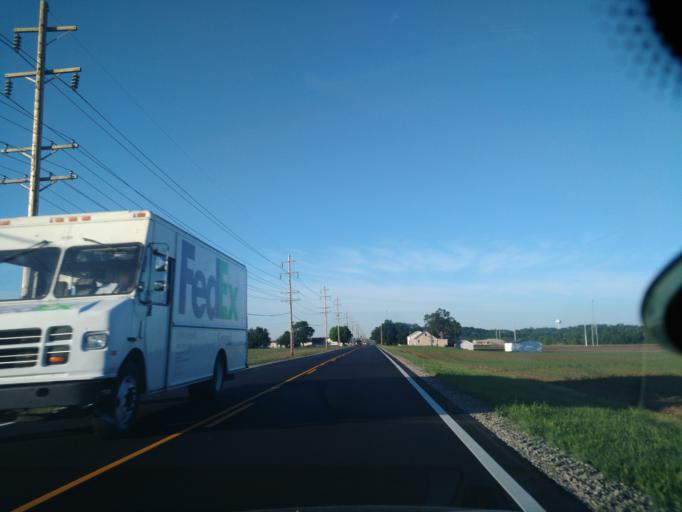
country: US
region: Ohio
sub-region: Ross County
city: Kingston
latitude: 39.4192
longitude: -82.9559
